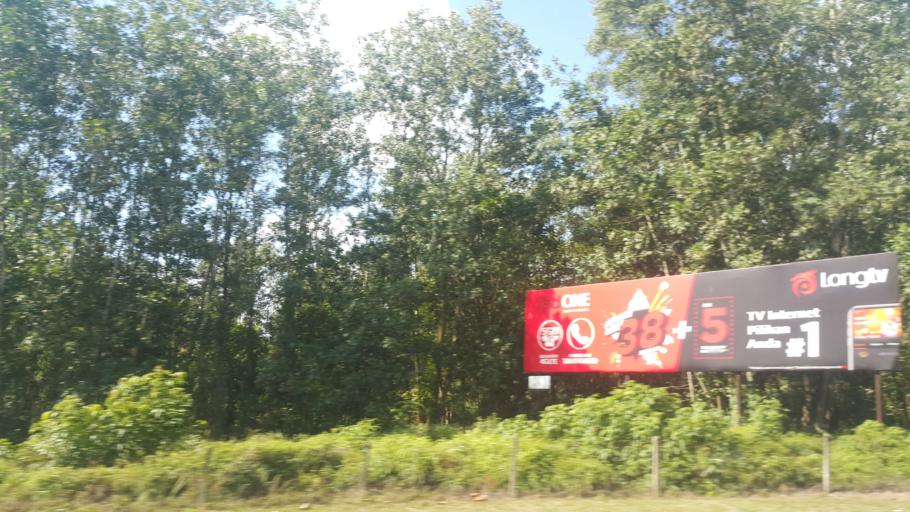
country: MY
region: Johor
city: Parit Raja
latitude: 1.9343
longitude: 103.1727
